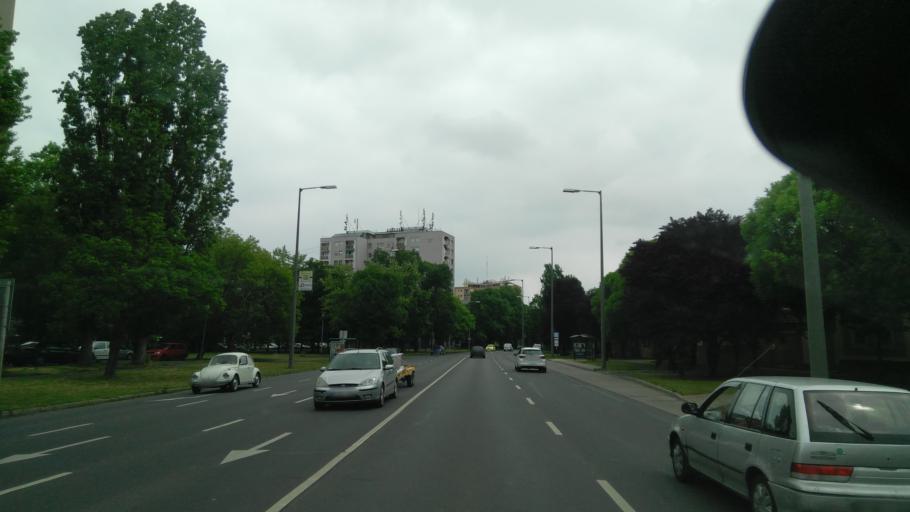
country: HU
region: Bekes
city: Bekescsaba
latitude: 46.6739
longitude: 21.0920
